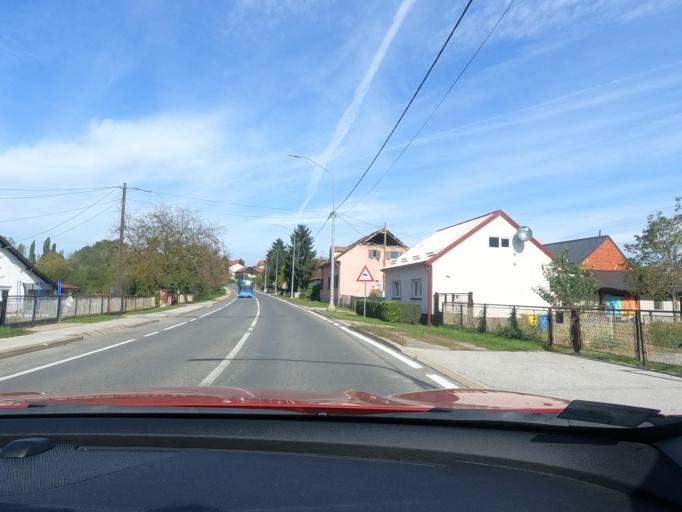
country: HR
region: Sisacko-Moslavacka
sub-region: Grad Sisak
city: Sisak
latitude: 45.4634
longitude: 16.3722
